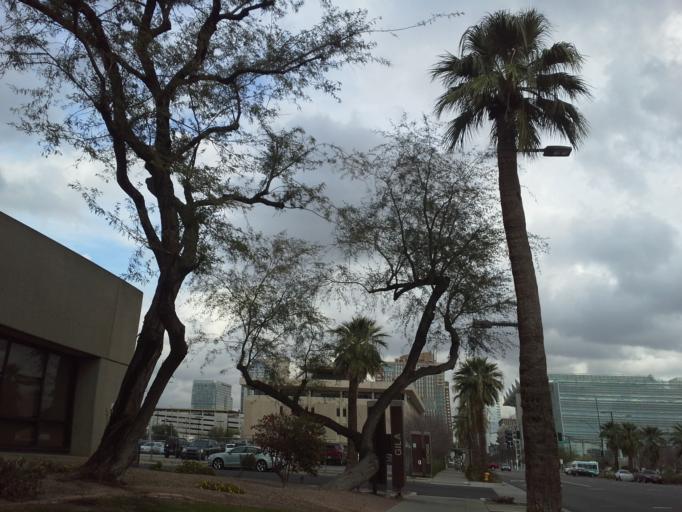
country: US
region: Arizona
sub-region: Maricopa County
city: Phoenix
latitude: 33.4483
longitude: -112.0841
